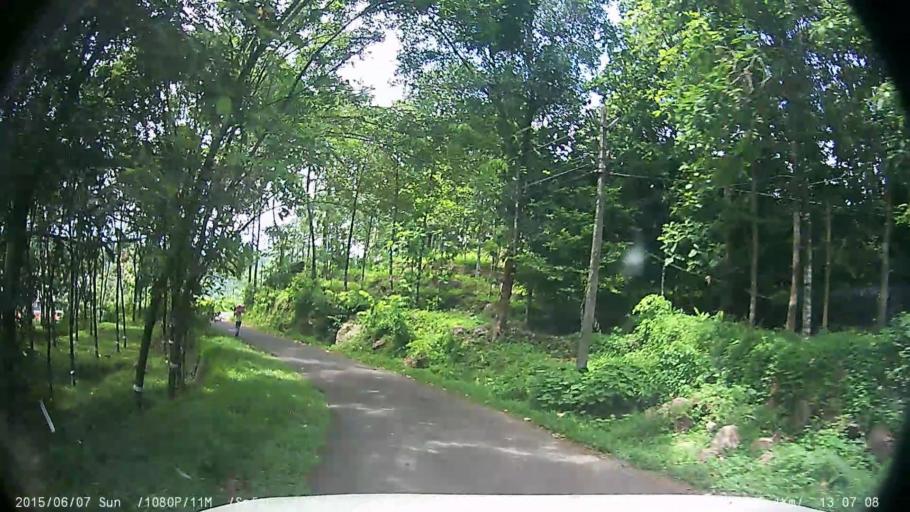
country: IN
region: Kerala
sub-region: Ernakulam
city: Muvattupuzha
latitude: 9.9279
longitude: 76.5758
